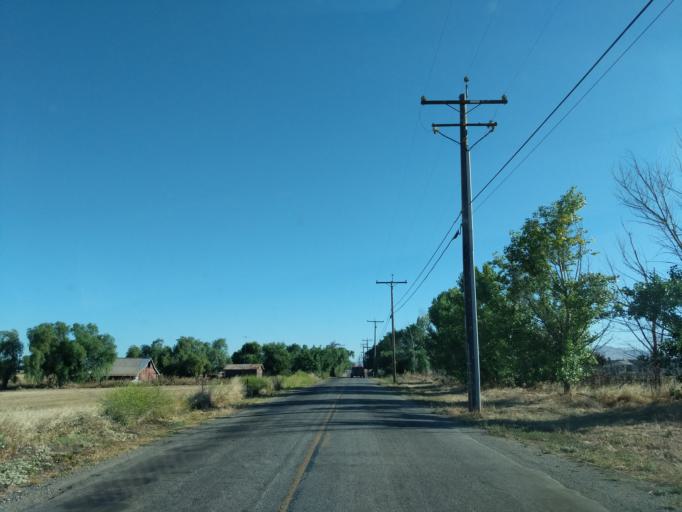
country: US
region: California
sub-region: San Benito County
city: Ridgemark
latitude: 36.8212
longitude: -121.3455
